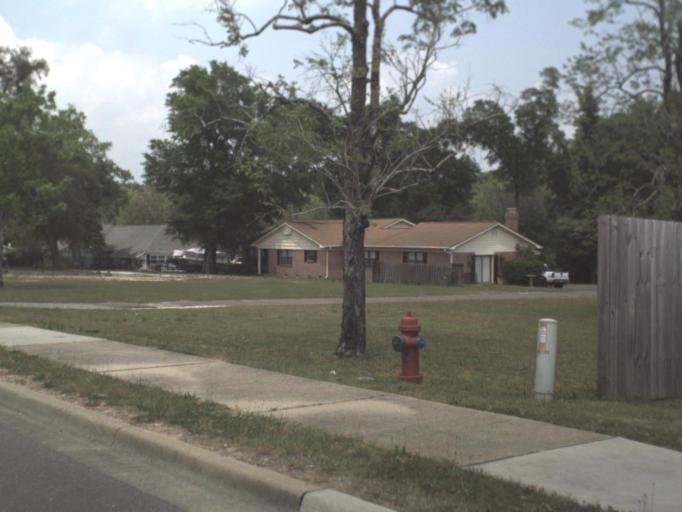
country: US
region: Florida
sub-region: Santa Rosa County
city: Milton
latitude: 30.6342
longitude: -87.0555
